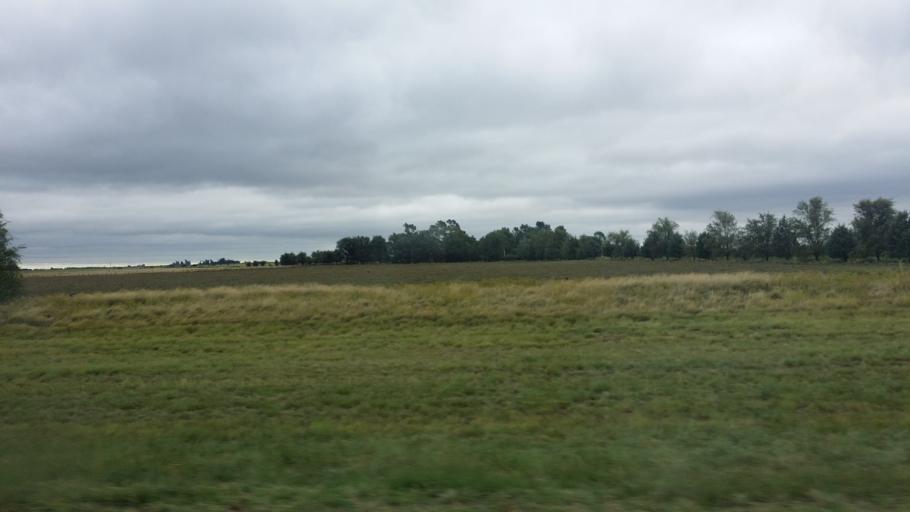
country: AR
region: La Pampa
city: Lonquimay
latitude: -36.4971
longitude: -63.6778
